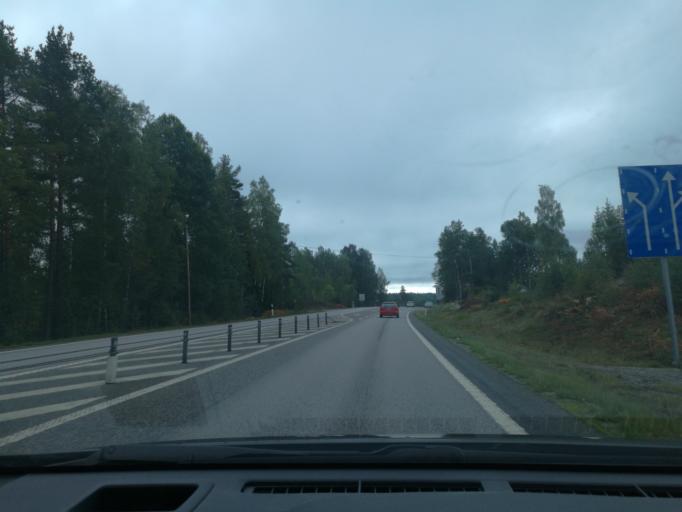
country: SE
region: OEstergoetland
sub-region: Norrkopings Kommun
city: Jursla
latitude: 58.7633
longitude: 16.1718
